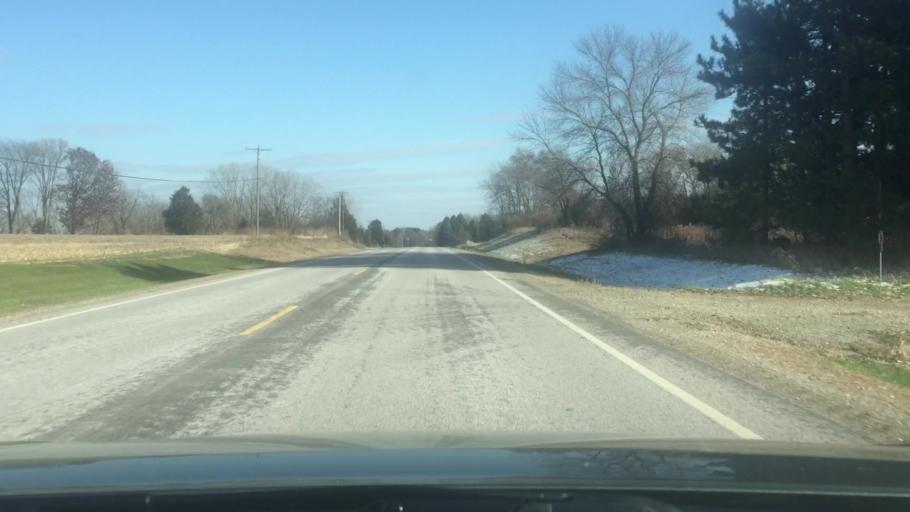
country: US
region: Wisconsin
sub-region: Jefferson County
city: Lake Koshkonong
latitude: 42.9485
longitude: -88.9015
